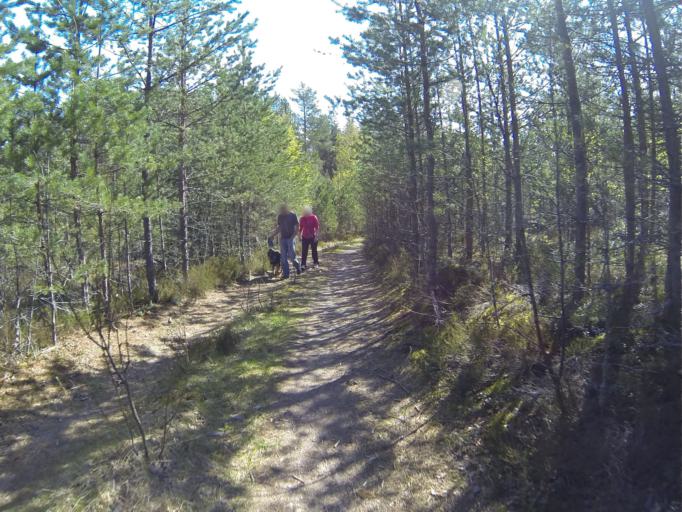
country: FI
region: Varsinais-Suomi
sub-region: Salo
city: Salo
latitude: 60.3941
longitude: 23.2004
